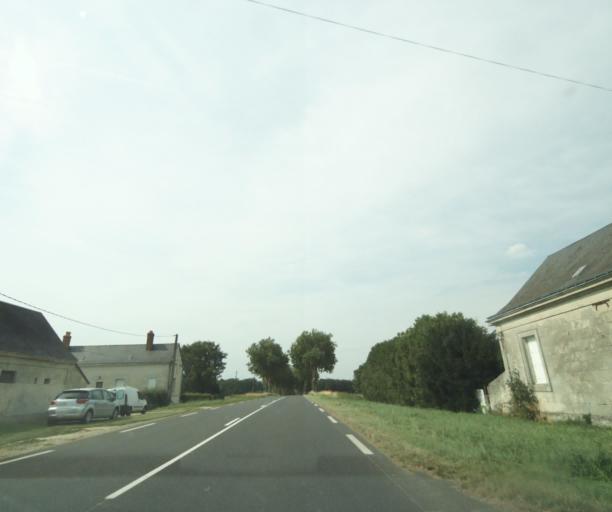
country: FR
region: Centre
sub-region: Departement d'Indre-et-Loire
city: Neuille-Pont-Pierre
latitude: 47.5727
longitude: 0.5456
